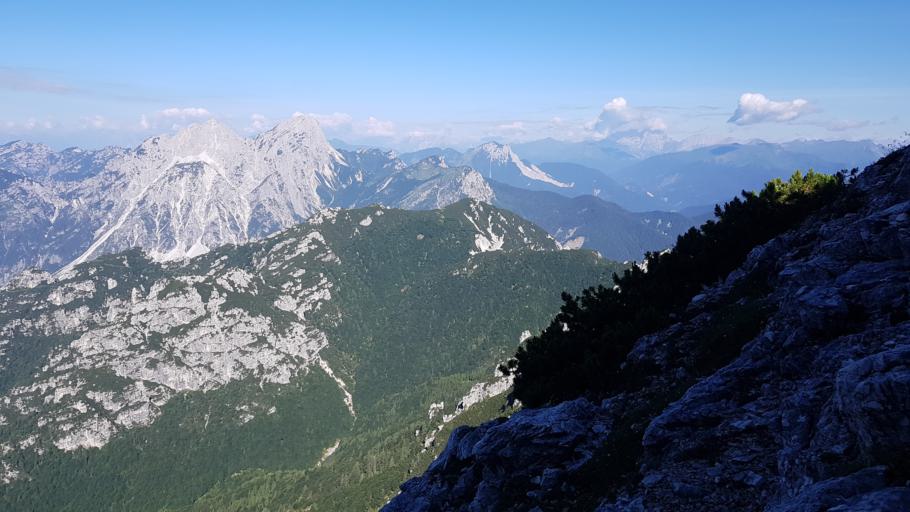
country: IT
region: Friuli Venezia Giulia
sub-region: Provincia di Udine
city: Pontebba
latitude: 46.4716
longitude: 13.2457
